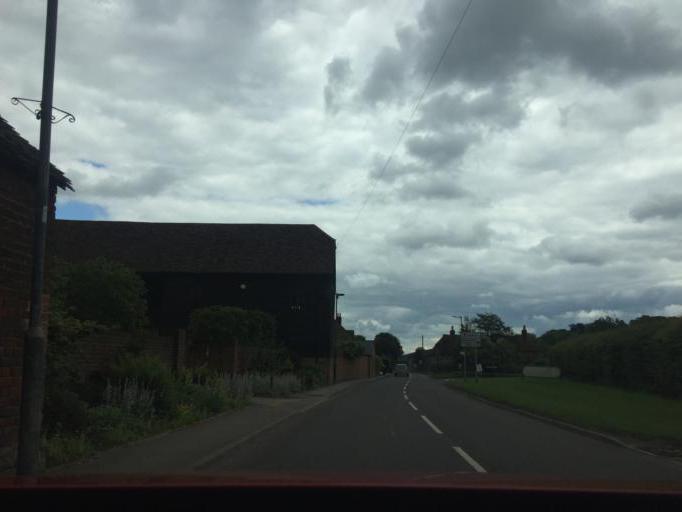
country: GB
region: England
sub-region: Hertfordshire
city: Wheathampstead
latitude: 51.8517
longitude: -0.2894
